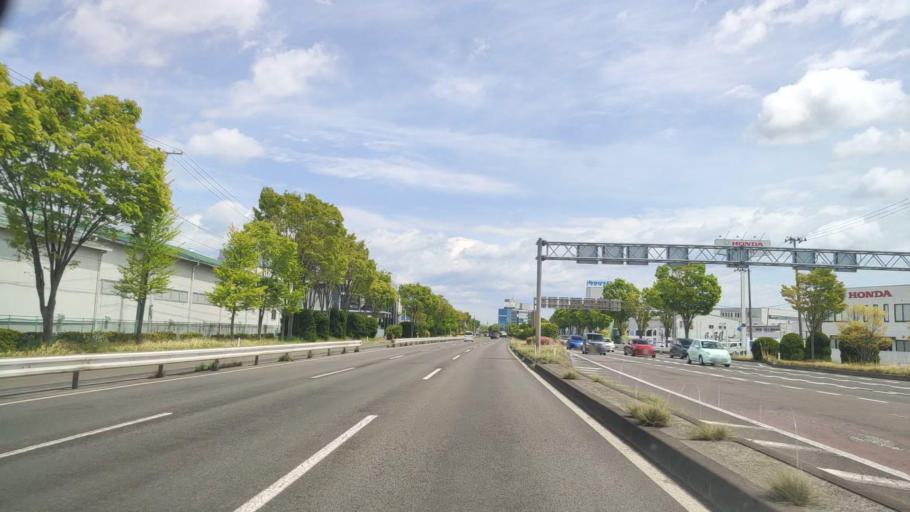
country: JP
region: Miyagi
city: Sendai-shi
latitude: 38.2520
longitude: 140.9294
